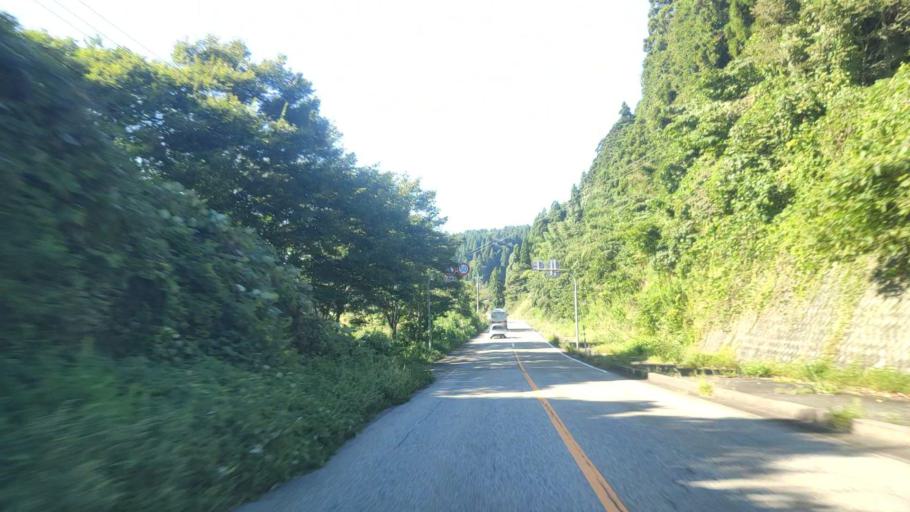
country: JP
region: Ishikawa
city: Nanao
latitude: 37.2746
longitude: 137.0544
